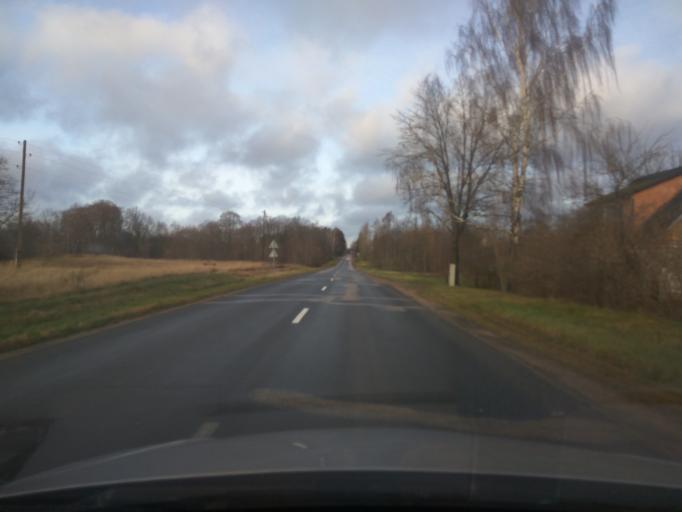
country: LV
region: Kuldigas Rajons
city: Kuldiga
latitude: 56.9677
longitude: 22.0018
